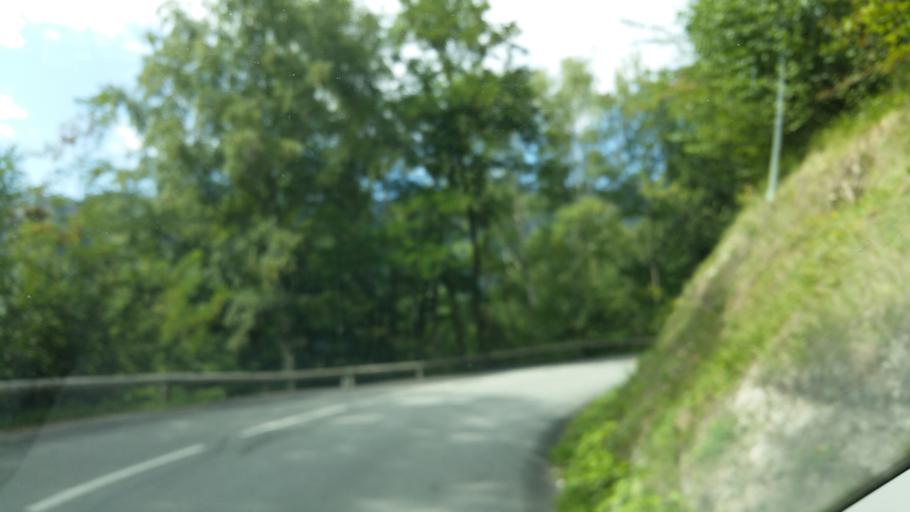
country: FR
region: Rhone-Alpes
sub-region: Departement de la Savoie
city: La Chambre
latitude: 45.3854
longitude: 6.3306
